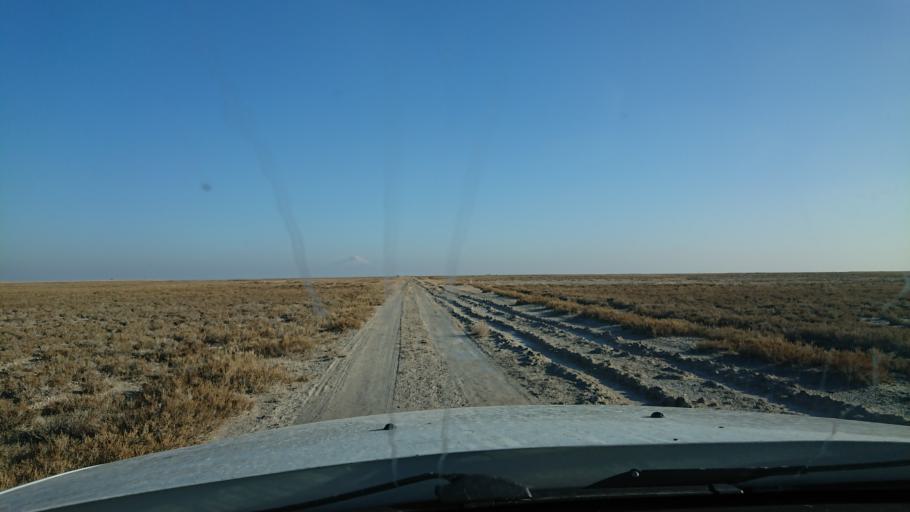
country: TR
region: Aksaray
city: Eskil
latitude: 38.4053
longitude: 33.5728
